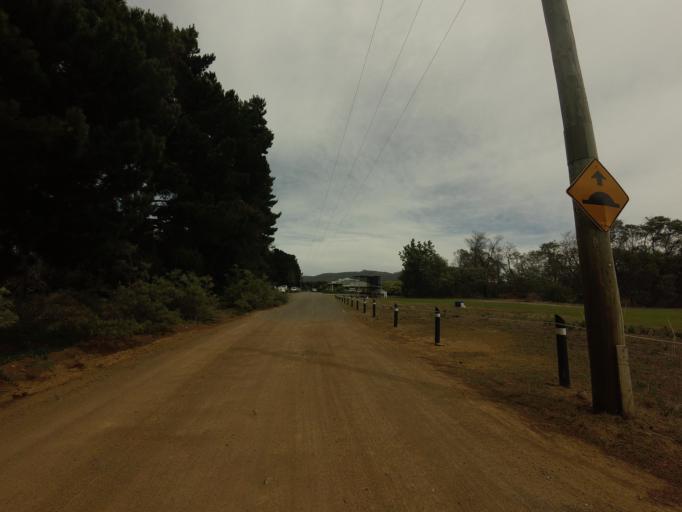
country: AU
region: Tasmania
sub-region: Clarence
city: Seven Mile Beach
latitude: -42.8459
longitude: 147.5103
